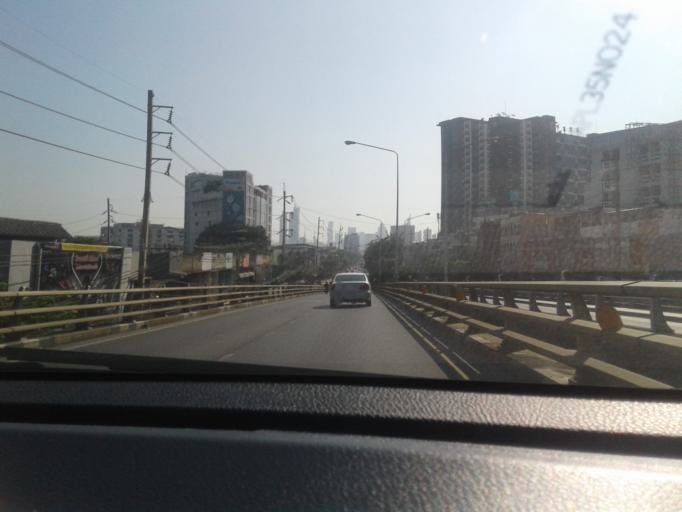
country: TH
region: Bangkok
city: Bangkok Yai
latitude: 13.7293
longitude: 100.4755
